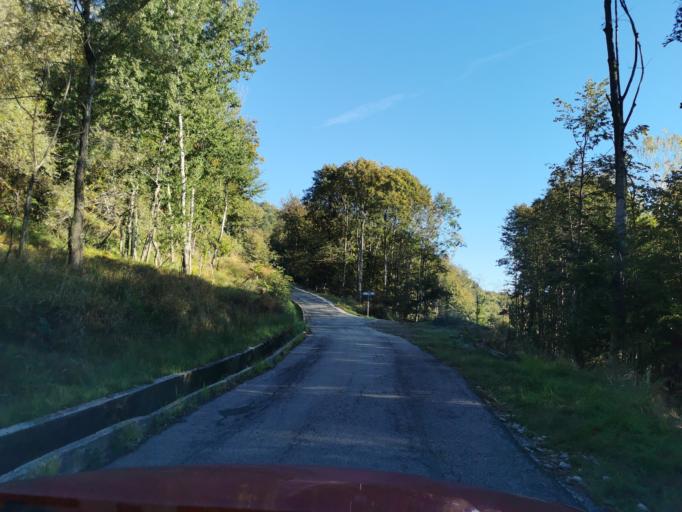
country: IT
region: Lombardy
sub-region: Provincia di Como
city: San Siro
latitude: 46.0685
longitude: 9.2553
